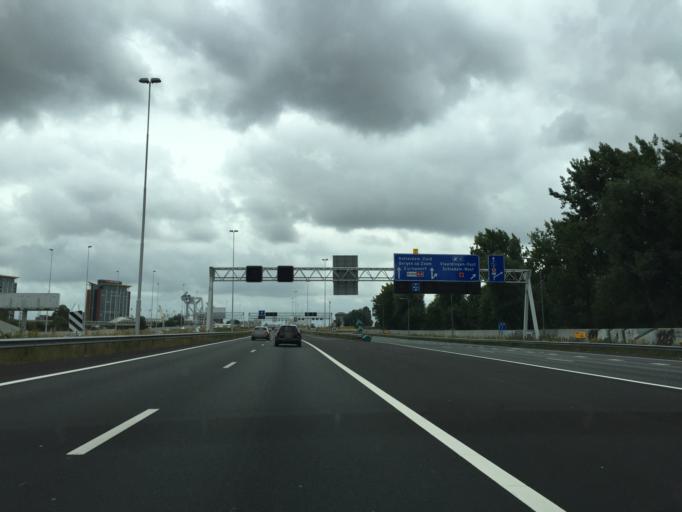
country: NL
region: South Holland
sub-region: Gemeente Schiedam
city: Schiedam
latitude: 51.9133
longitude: 4.3682
